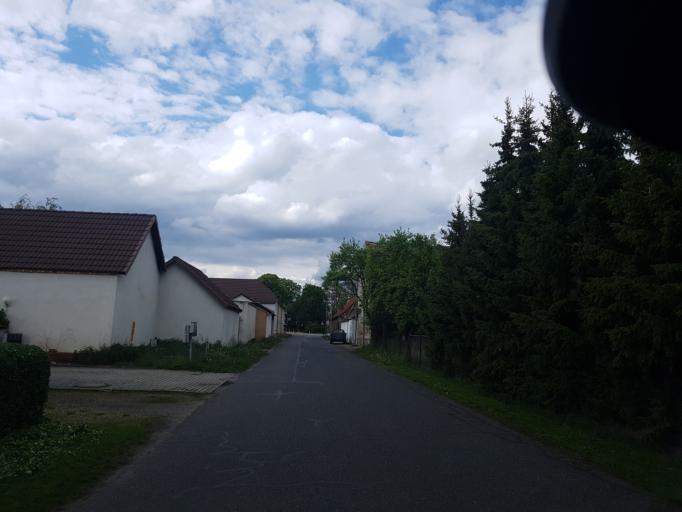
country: DE
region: Brandenburg
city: Grossraschen
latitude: 51.5866
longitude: 14.0620
